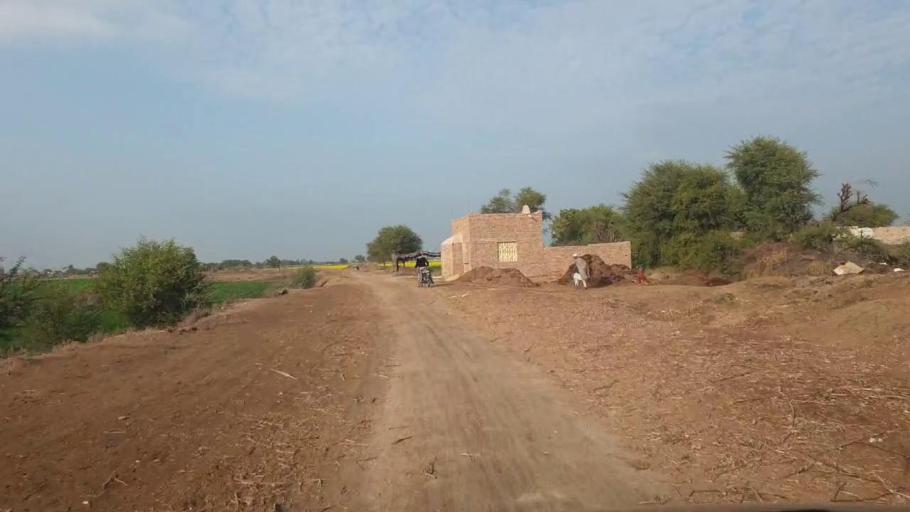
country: PK
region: Sindh
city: Shahdadpur
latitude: 25.8777
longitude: 68.7162
